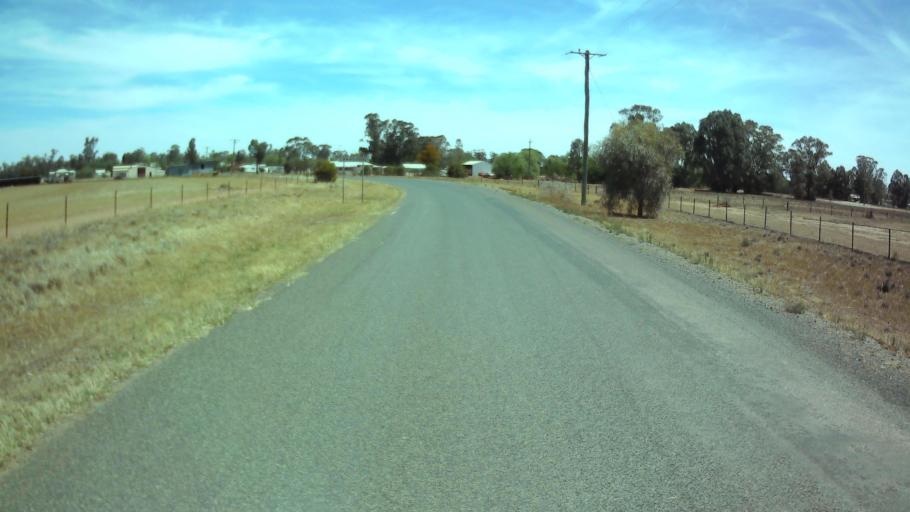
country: AU
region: New South Wales
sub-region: Weddin
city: Grenfell
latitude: -33.8384
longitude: 147.7453
